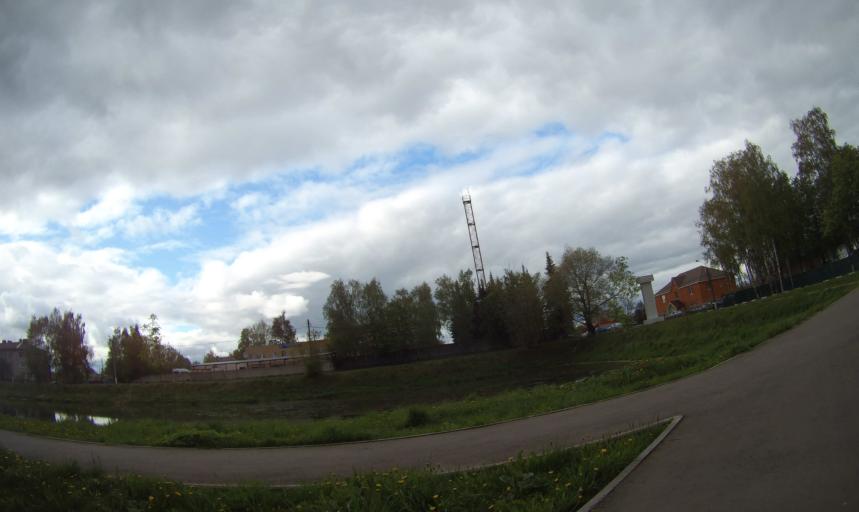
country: RU
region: Moskovskaya
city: Rechitsy
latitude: 55.5875
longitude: 38.5030
